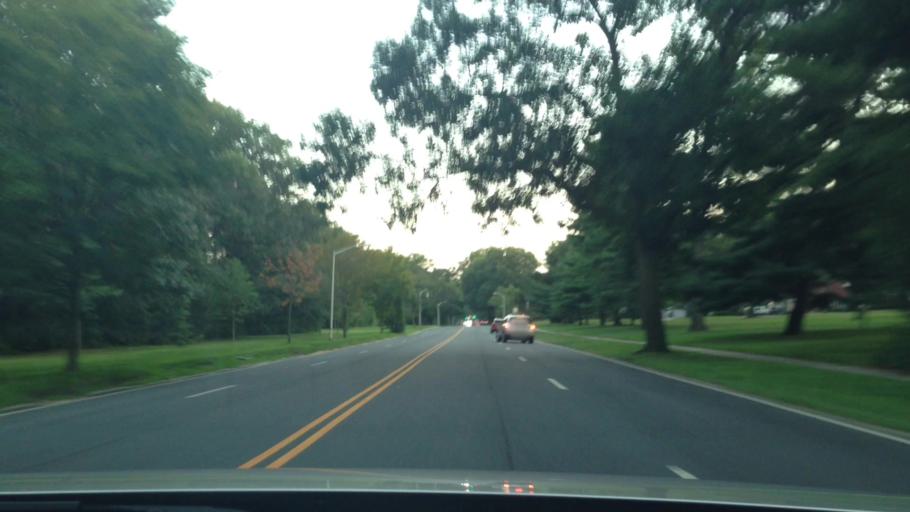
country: US
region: New York
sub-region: Nassau County
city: Carle Place
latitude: 40.7385
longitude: -73.6181
